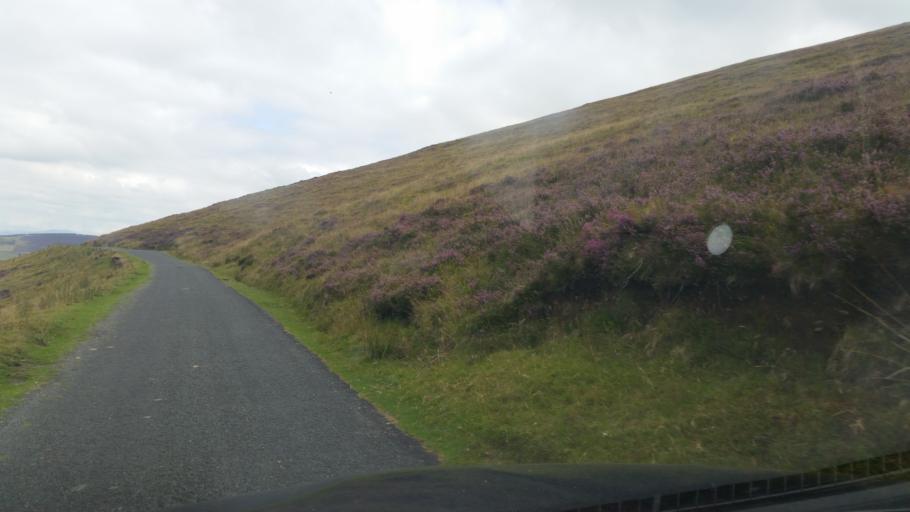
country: IE
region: Leinster
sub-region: Loch Garman
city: Bunclody
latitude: 52.6377
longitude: -6.7897
